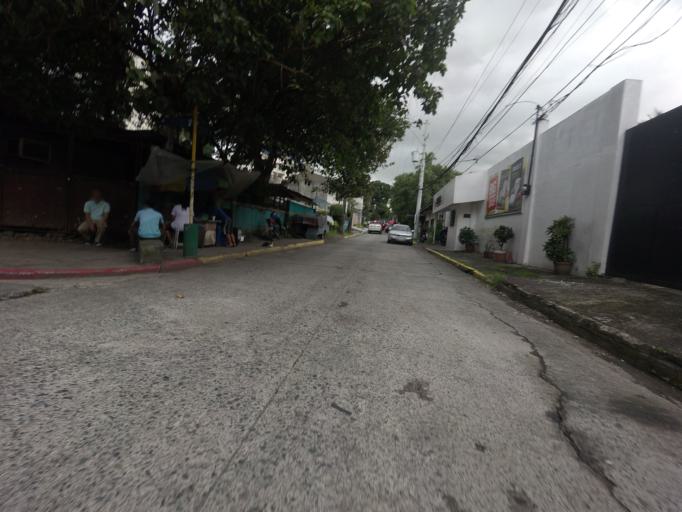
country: PH
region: Metro Manila
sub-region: Mandaluyong
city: Mandaluyong City
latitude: 14.5906
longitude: 121.0448
